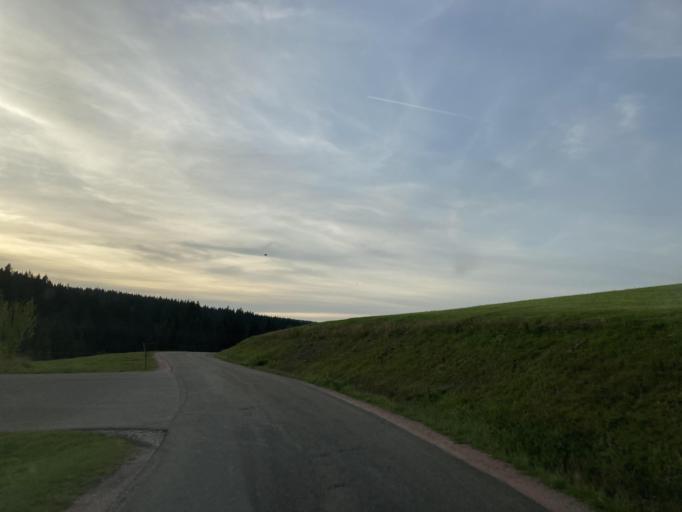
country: DE
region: Baden-Wuerttemberg
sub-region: Freiburg Region
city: Schonwald im Schwarzwald
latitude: 48.1004
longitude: 8.1737
